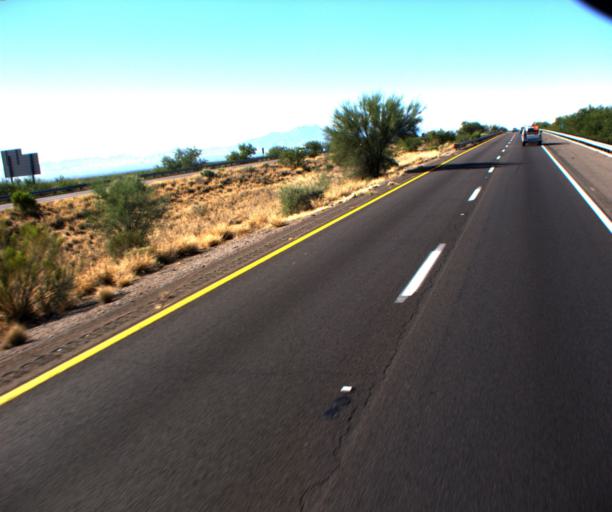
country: US
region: Arizona
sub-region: Pima County
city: Summit
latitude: 32.0537
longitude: -110.9930
